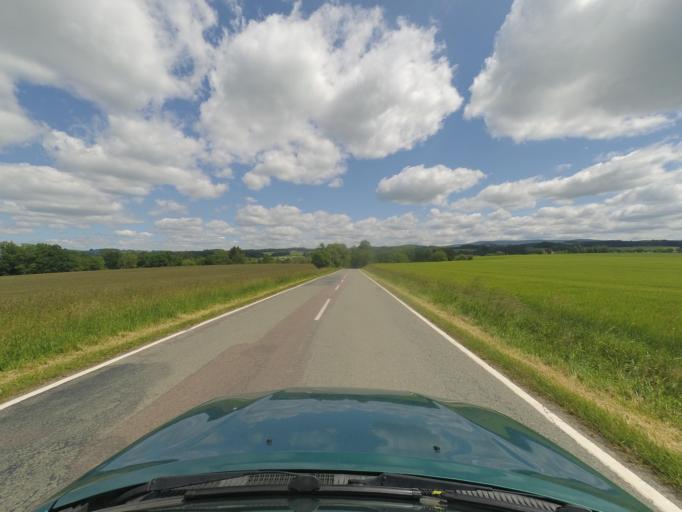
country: CZ
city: Dobruska
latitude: 50.3203
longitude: 16.2023
